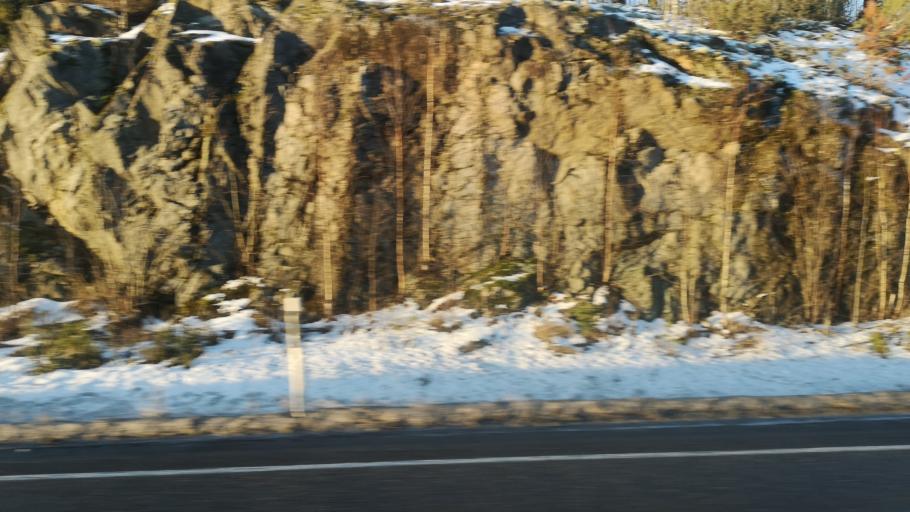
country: FI
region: Southern Savonia
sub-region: Pieksaemaeki
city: Juva
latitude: 61.7616
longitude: 27.5758
